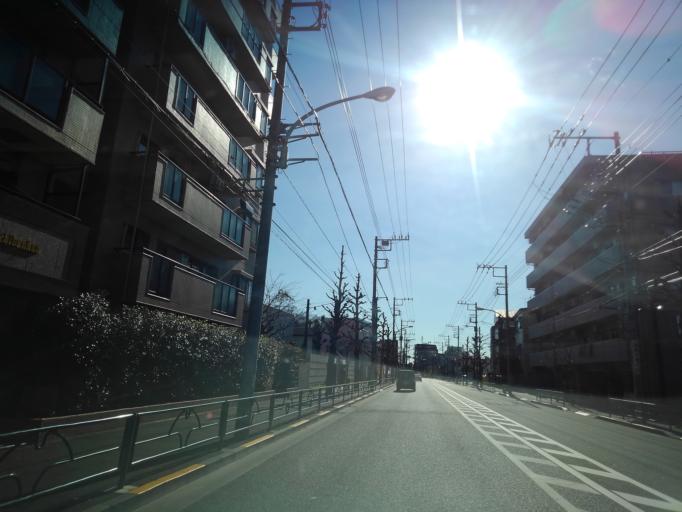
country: JP
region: Tokyo
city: Kokubunji
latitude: 35.6830
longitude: 139.4992
